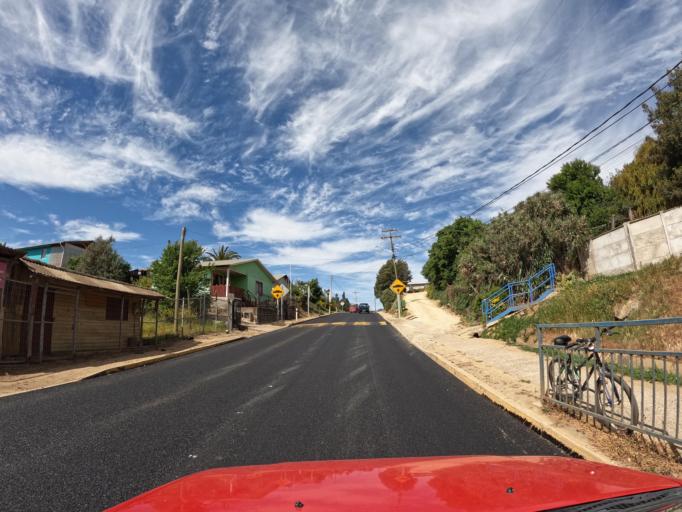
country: CL
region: Maule
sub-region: Provincia de Talca
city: Constitucion
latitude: -35.0977
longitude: -72.0120
